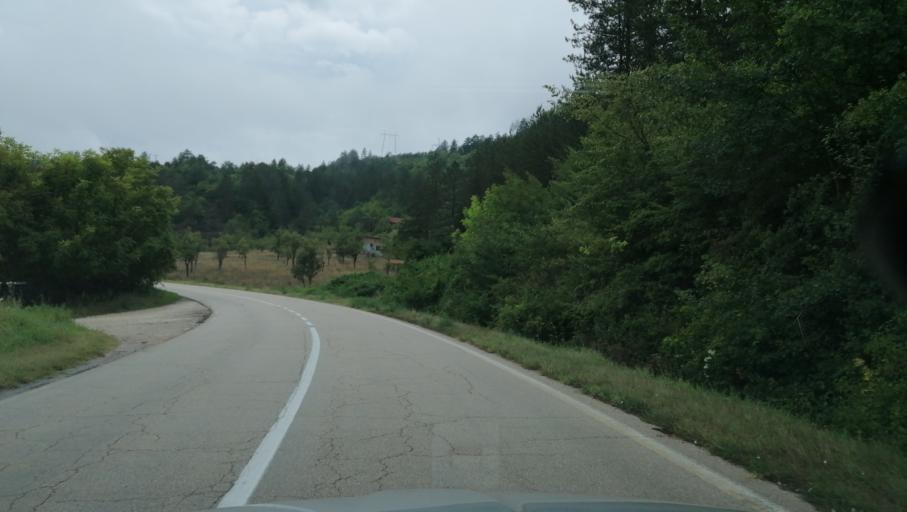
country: BA
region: Republika Srpska
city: Visegrad
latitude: 43.7874
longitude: 19.3312
